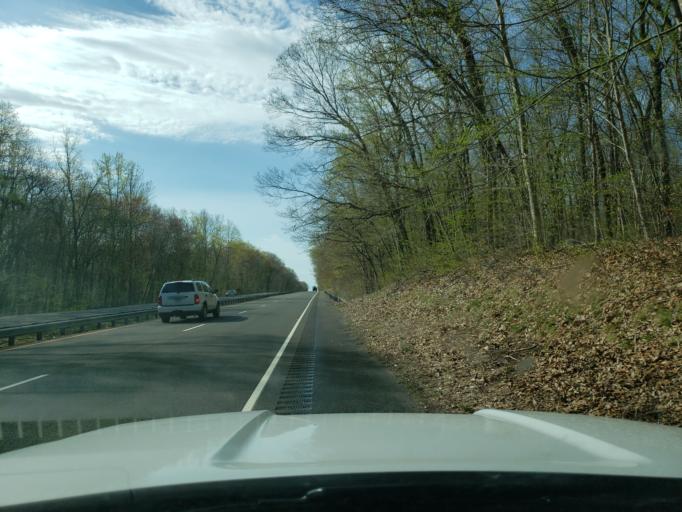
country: US
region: Connecticut
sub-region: New Haven County
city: Madison
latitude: 41.2866
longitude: -72.5681
